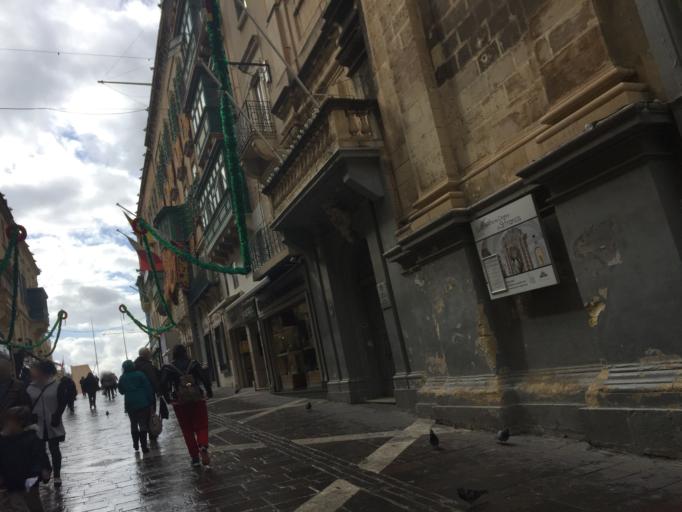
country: MT
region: Il-Furjana
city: Floriana
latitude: 35.8972
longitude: 14.5109
